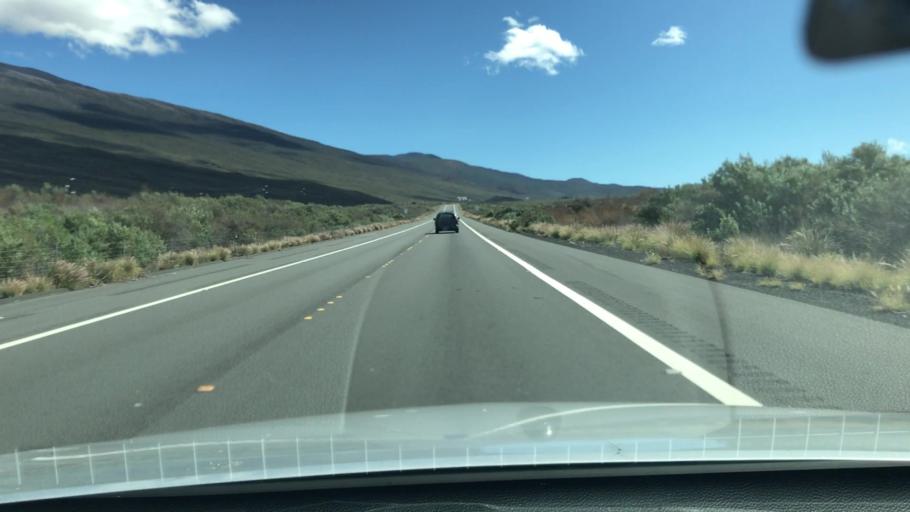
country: US
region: Hawaii
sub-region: Hawaii County
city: Waimea
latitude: 19.7655
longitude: -155.5686
